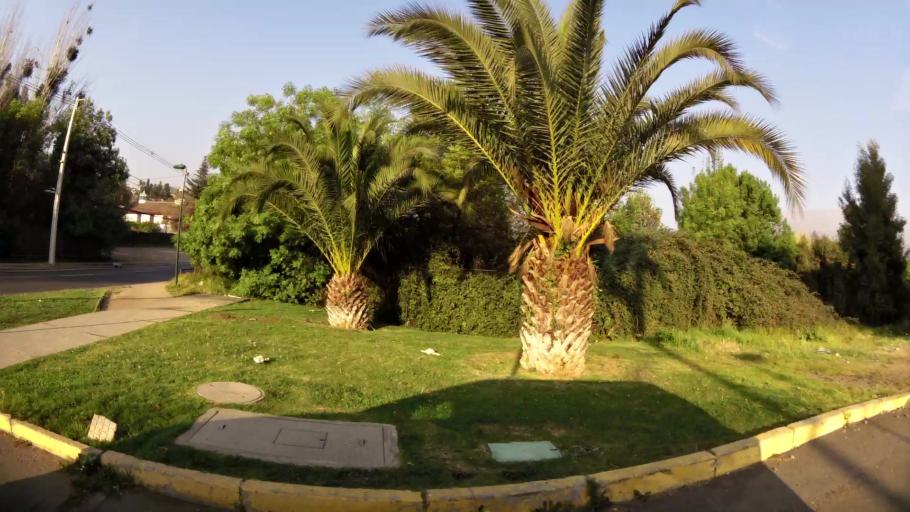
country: CL
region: Santiago Metropolitan
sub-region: Provincia de Santiago
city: Villa Presidente Frei, Nunoa, Santiago, Chile
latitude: -33.3513
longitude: -70.5079
